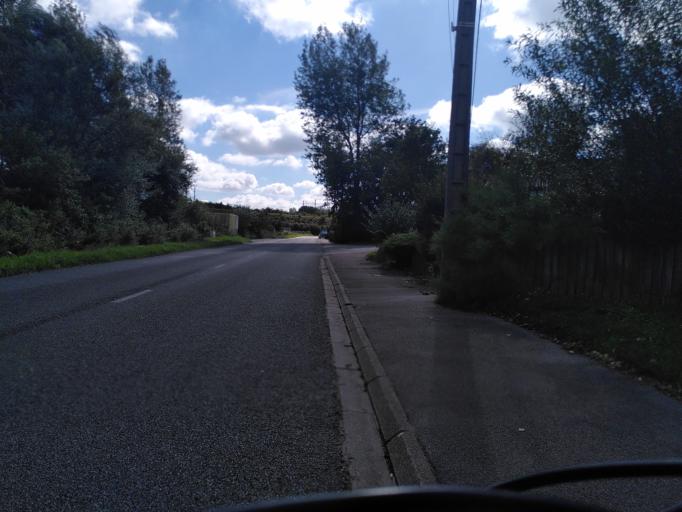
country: FR
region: Nord-Pas-de-Calais
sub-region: Departement du Pas-de-Calais
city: Wimille
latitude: 50.7828
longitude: 1.6328
